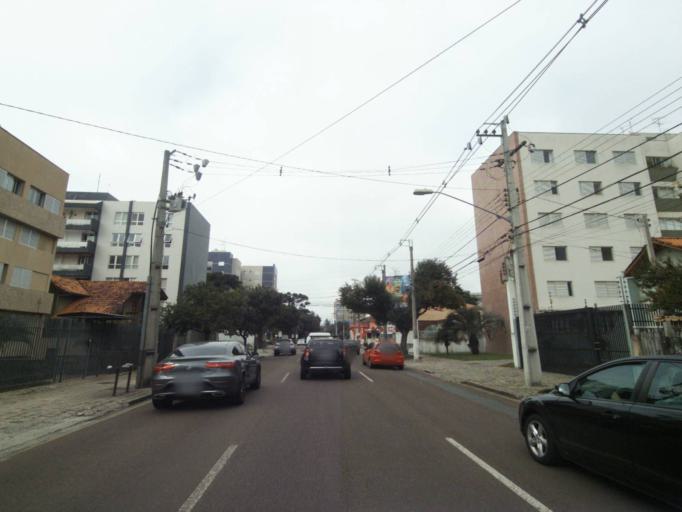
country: BR
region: Parana
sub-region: Curitiba
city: Curitiba
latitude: -25.4200
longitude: -49.2543
